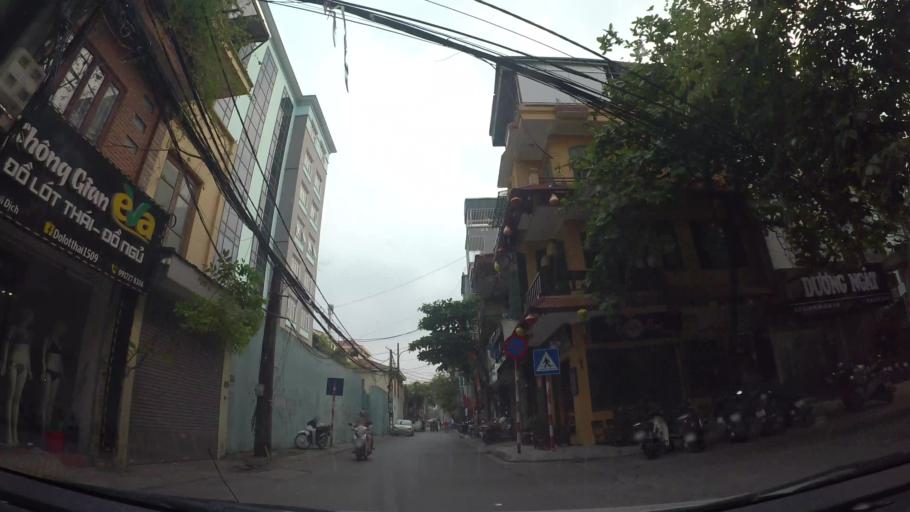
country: VN
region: Ha Noi
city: Cau Dien
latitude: 21.0391
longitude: 105.7741
